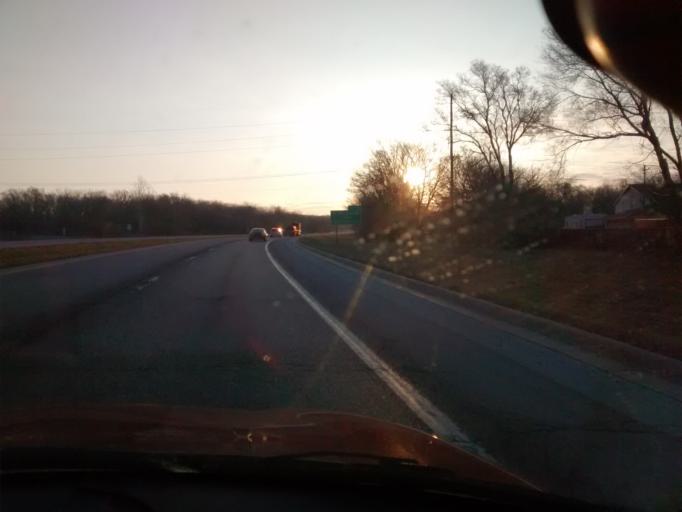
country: US
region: Iowa
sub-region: Pottawattamie County
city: Carter Lake
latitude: 41.2747
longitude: -95.8918
